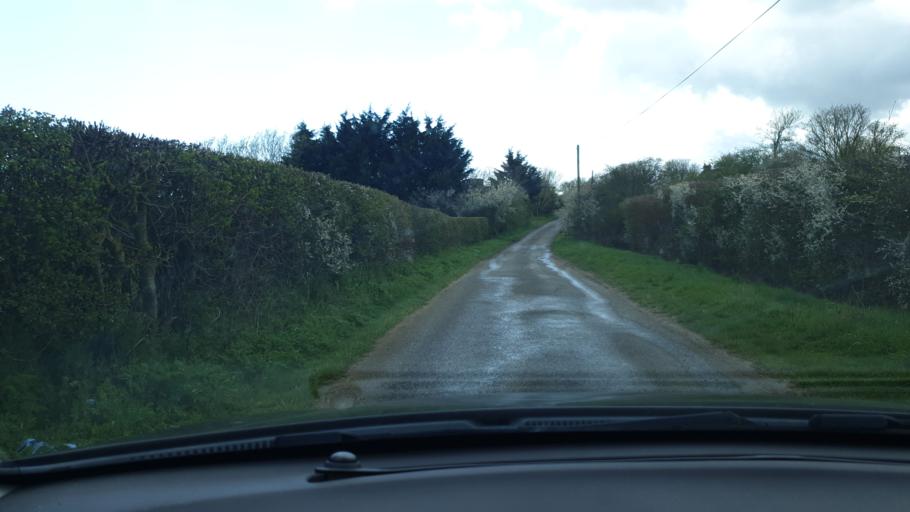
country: GB
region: England
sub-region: Essex
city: Little Clacton
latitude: 51.8934
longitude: 1.1316
